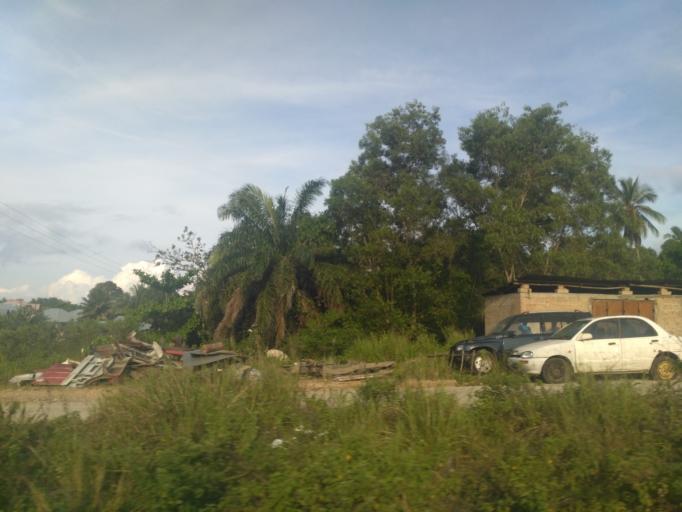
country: TZ
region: Zanzibar Urban/West
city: Zanzibar
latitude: -6.1542
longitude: 39.2353
